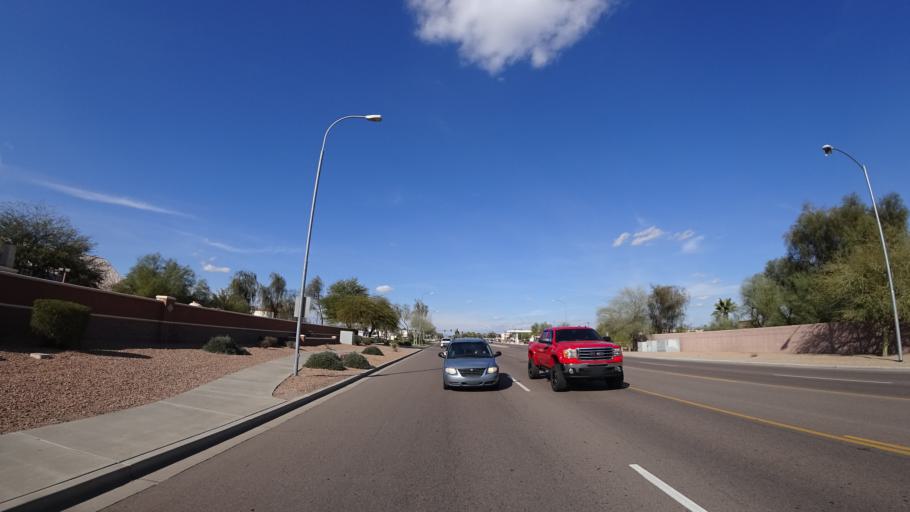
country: US
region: Arizona
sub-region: Maricopa County
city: Peoria
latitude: 33.6081
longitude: -112.2202
